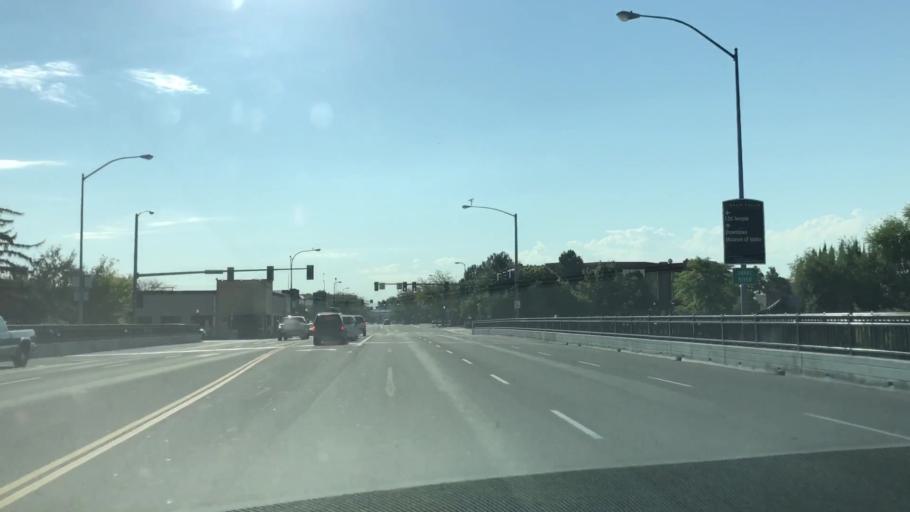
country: US
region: Idaho
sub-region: Bonneville County
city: Idaho Falls
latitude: 43.4931
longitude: -112.0449
